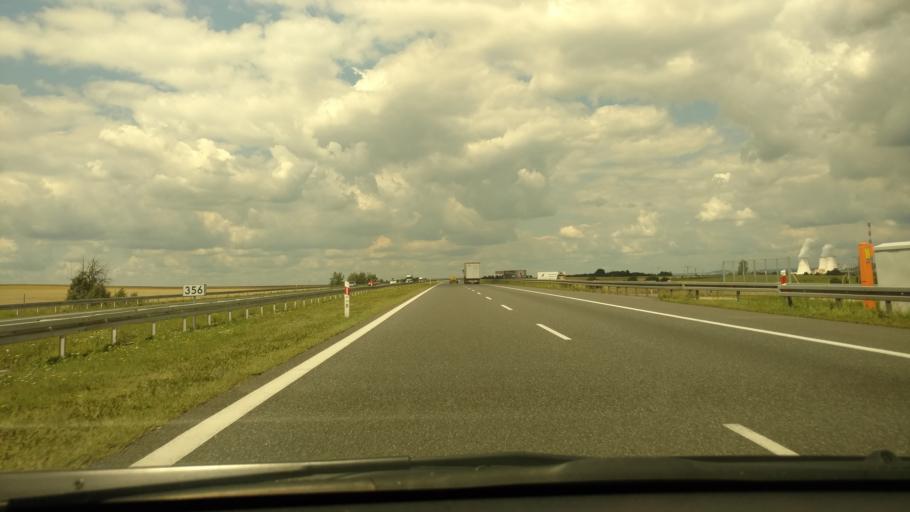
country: PL
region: Silesian Voivodeship
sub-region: Powiat bierunsko-ledzinski
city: Imielin
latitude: 50.1651
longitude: 19.2205
